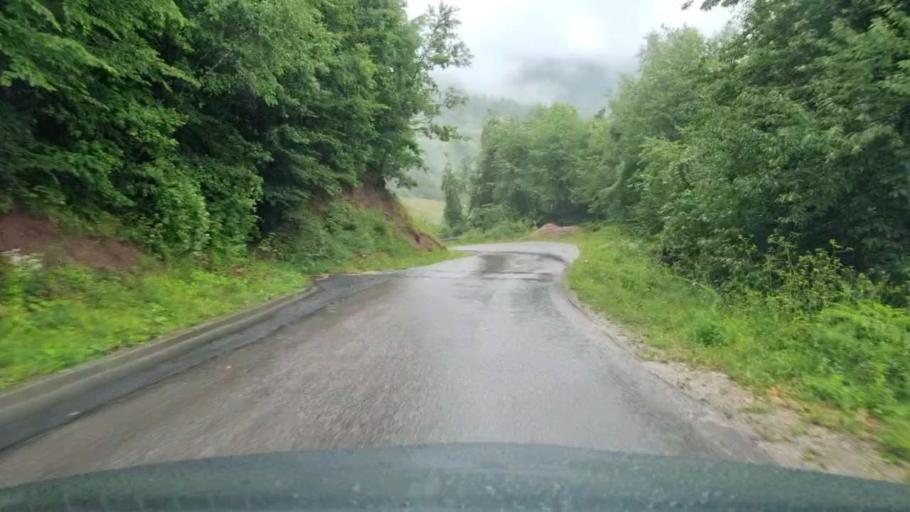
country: BA
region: Federation of Bosnia and Herzegovina
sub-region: Bosansko-Podrinjski Kanton
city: Ustikolina
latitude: 43.6338
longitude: 18.6270
